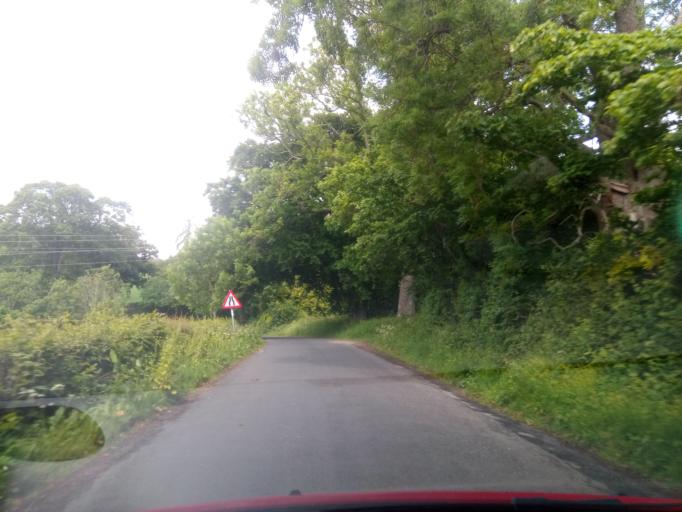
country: GB
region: Scotland
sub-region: The Scottish Borders
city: Selkirk
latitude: 55.5852
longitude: -2.8399
